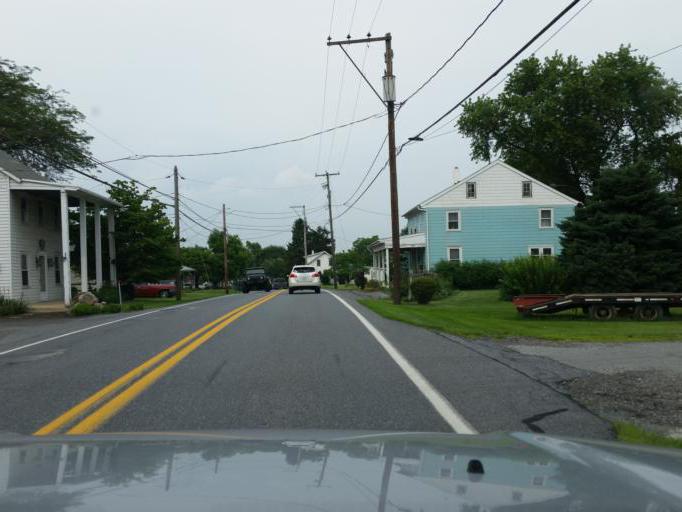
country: US
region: Pennsylvania
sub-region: Lancaster County
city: Manheim
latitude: 40.1455
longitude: -76.4174
